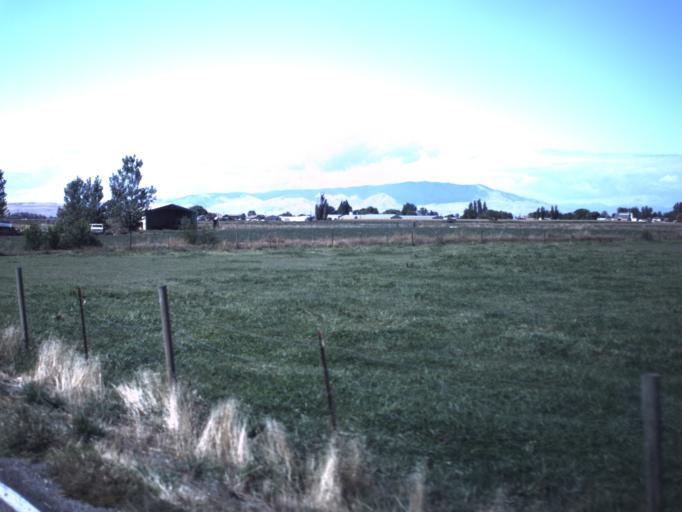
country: US
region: Utah
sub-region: Utah County
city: Benjamin
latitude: 40.1147
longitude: -111.7217
